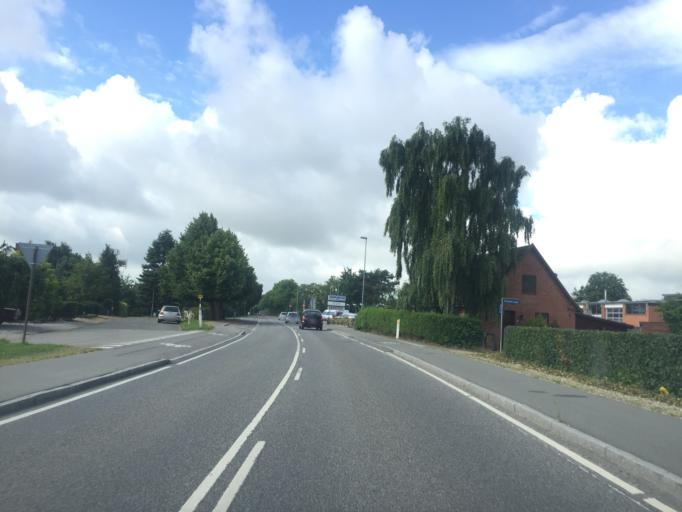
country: DK
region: South Denmark
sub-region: Svendborg Kommune
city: Thuro By
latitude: 55.0977
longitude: 10.7025
